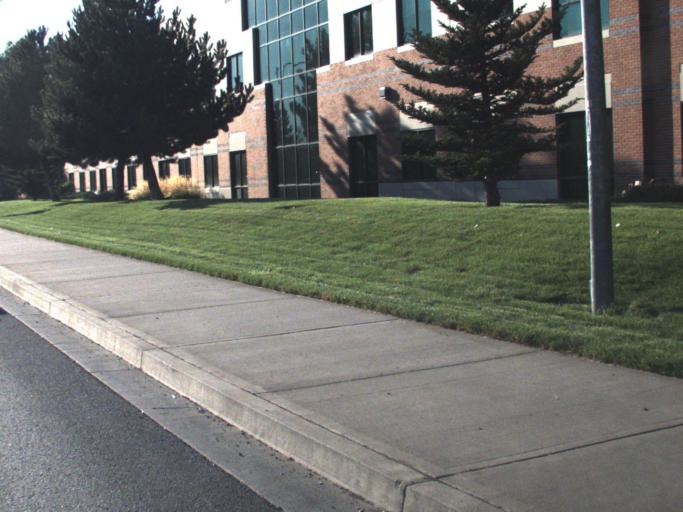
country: US
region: Washington
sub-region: Spokane County
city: Spokane
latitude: 47.6619
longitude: -117.3907
